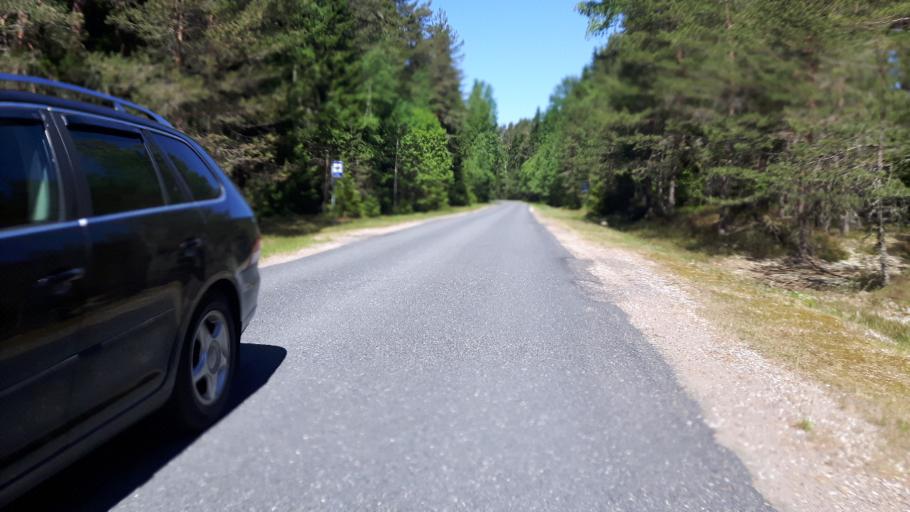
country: EE
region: Harju
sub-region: Loksa linn
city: Loksa
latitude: 59.5683
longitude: 25.6250
